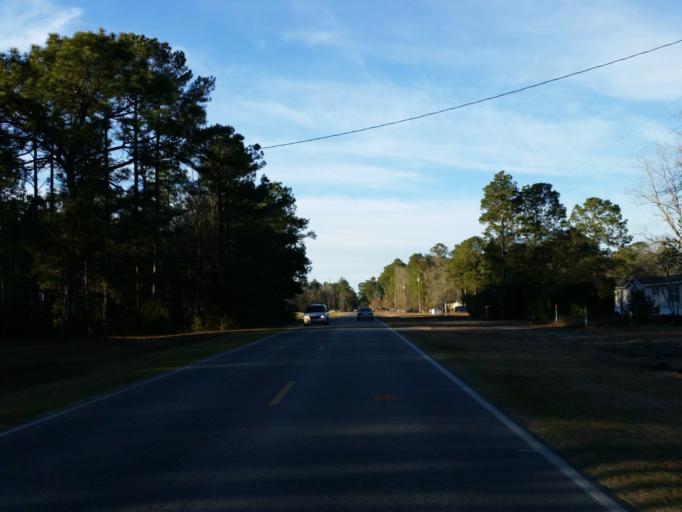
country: US
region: Georgia
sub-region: Cook County
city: Sparks
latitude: 31.2308
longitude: -83.4603
